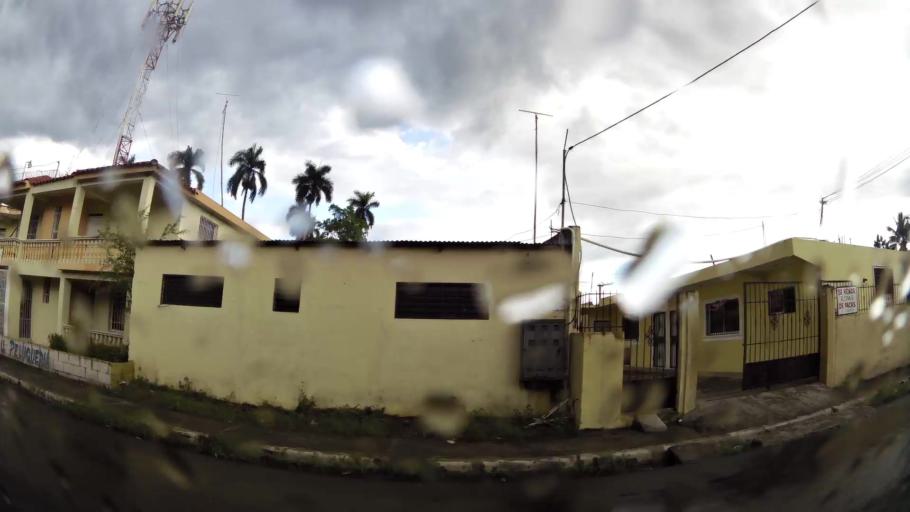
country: DO
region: Monsenor Nouel
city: Bonao
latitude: 18.9367
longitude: -70.4047
